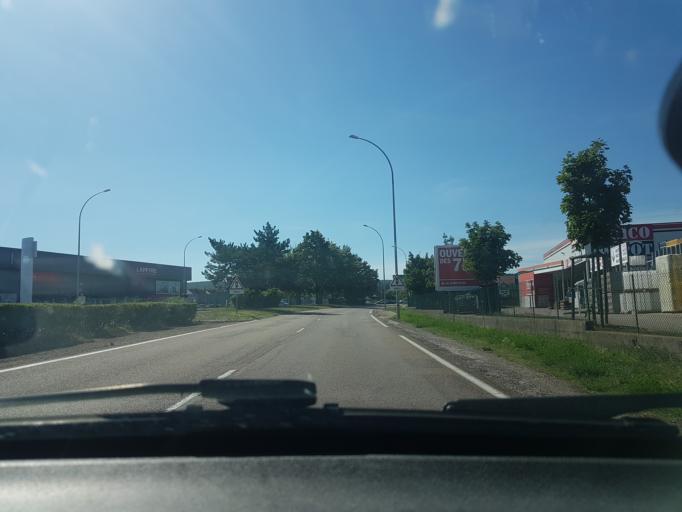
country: FR
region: Bourgogne
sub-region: Departement de la Cote-d'Or
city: Chenove
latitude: 47.2819
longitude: 5.0109
